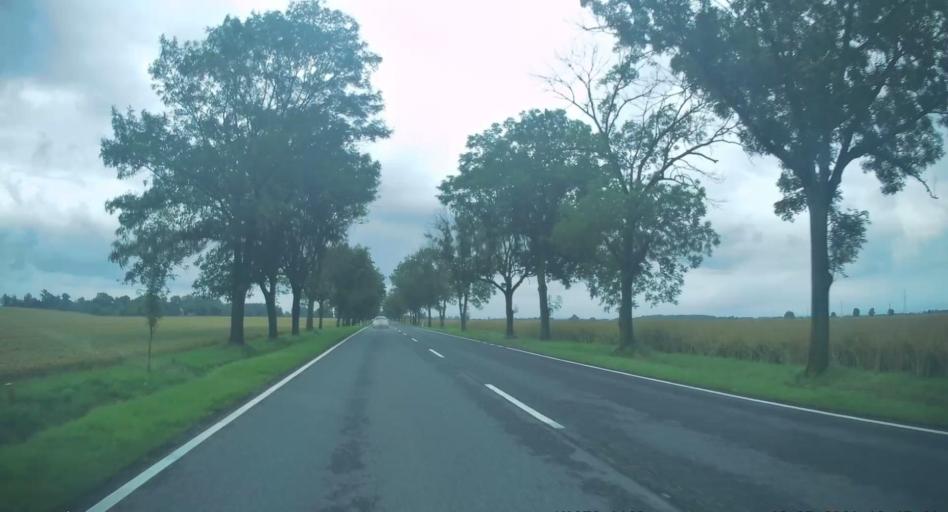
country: PL
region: Opole Voivodeship
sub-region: Powiat nyski
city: Paczkow
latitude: 50.4496
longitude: 17.0853
